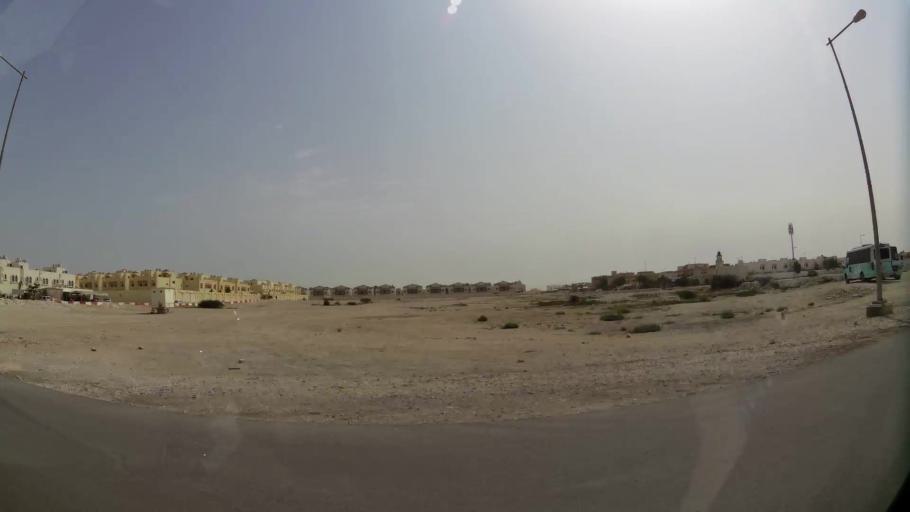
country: QA
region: Baladiyat ad Dawhah
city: Doha
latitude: 25.3020
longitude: 51.4795
